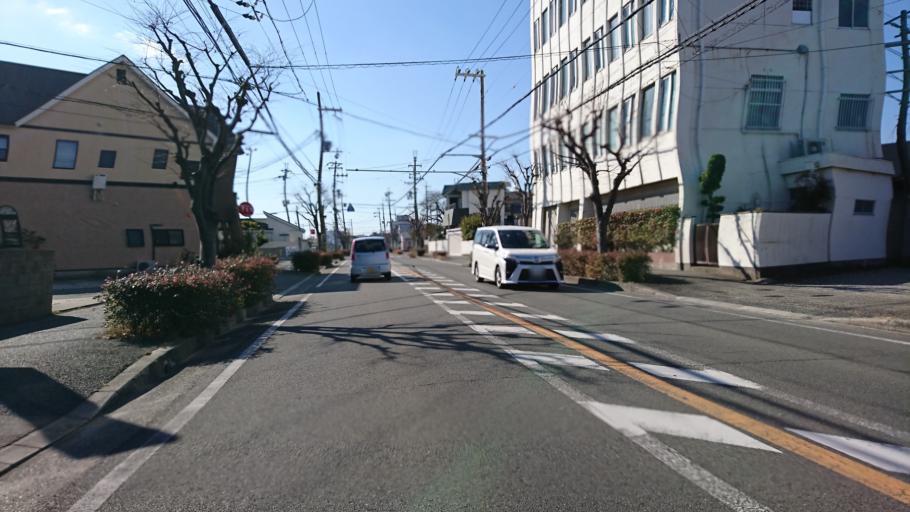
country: JP
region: Hyogo
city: Kakogawacho-honmachi
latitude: 34.7773
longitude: 134.8054
